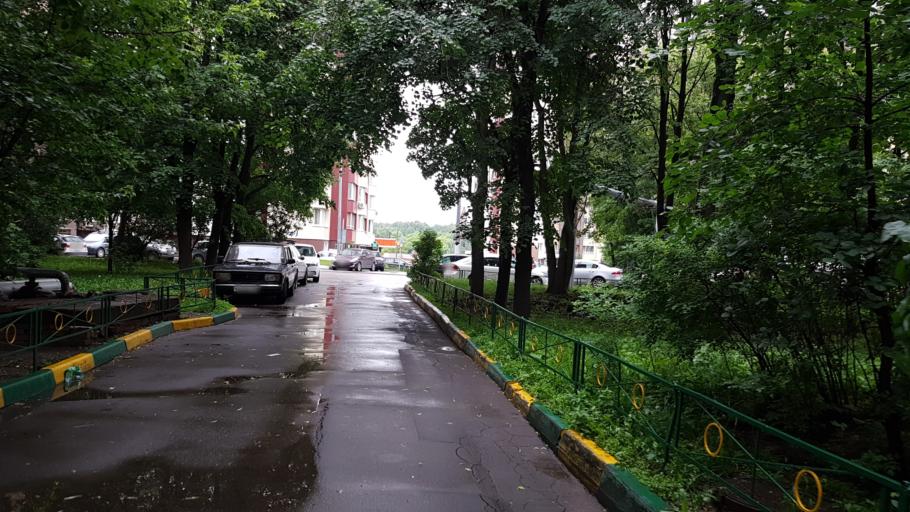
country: RU
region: Moscow
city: Khimki
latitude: 55.8878
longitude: 37.4551
